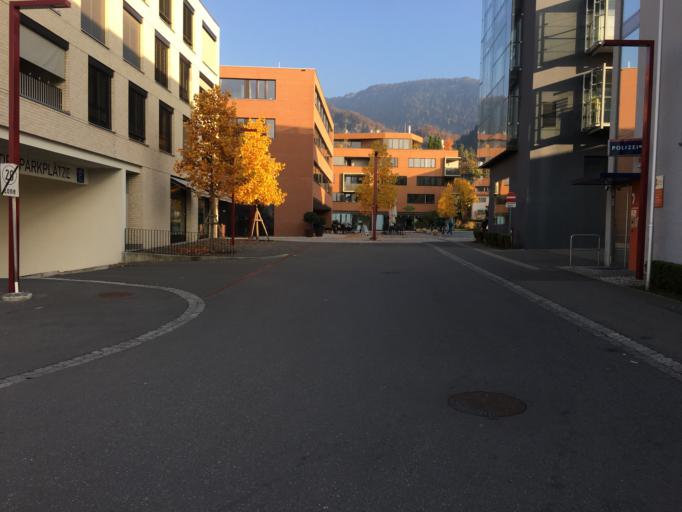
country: AT
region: Vorarlberg
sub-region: Politischer Bezirk Feldkirch
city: Gotzis
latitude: 47.3363
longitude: 9.6460
